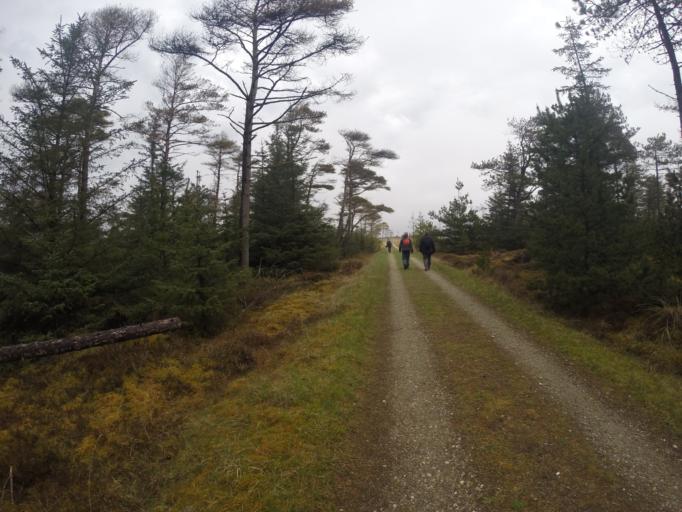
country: DK
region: North Denmark
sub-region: Thisted Kommune
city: Hanstholm
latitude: 57.0392
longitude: 8.5575
